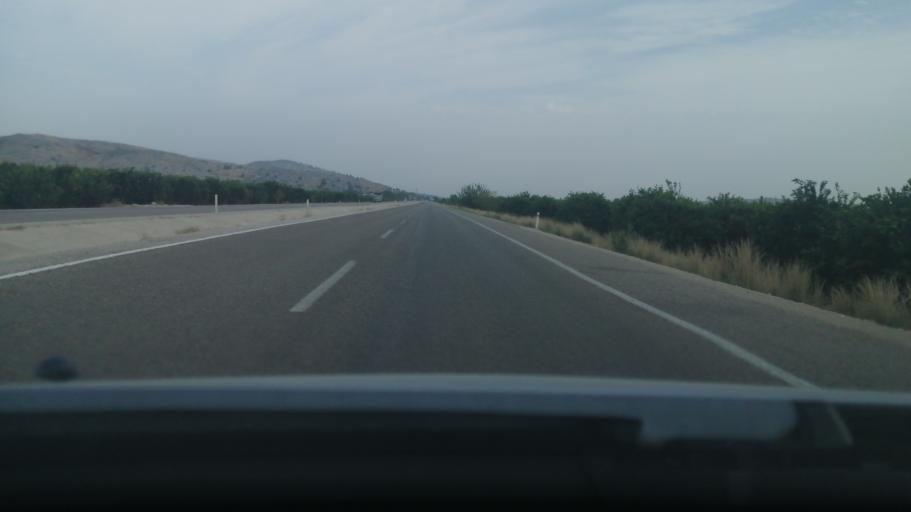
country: TR
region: Adana
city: Kozan
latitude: 37.3844
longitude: 35.8104
